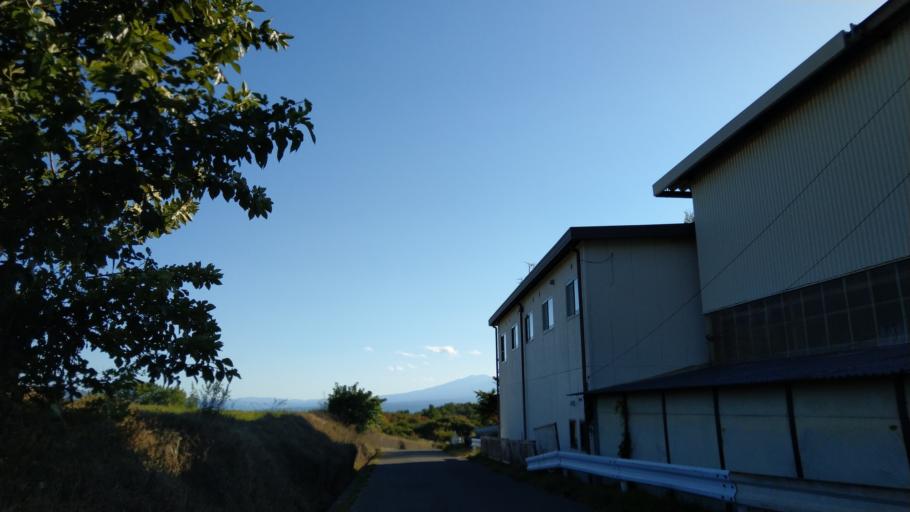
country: JP
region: Nagano
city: Komoro
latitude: 36.3443
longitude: 138.4322
